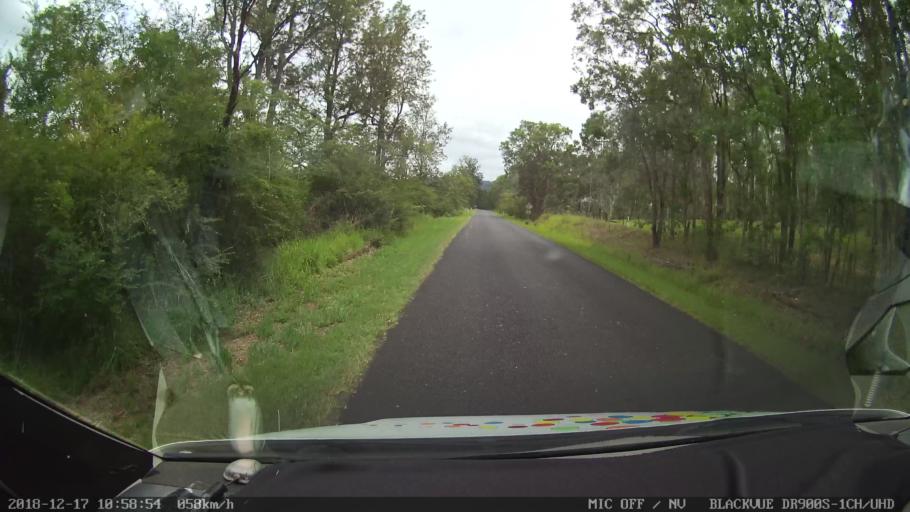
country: AU
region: New South Wales
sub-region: Richmond Valley
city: Casino
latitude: -28.8249
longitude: 152.6083
